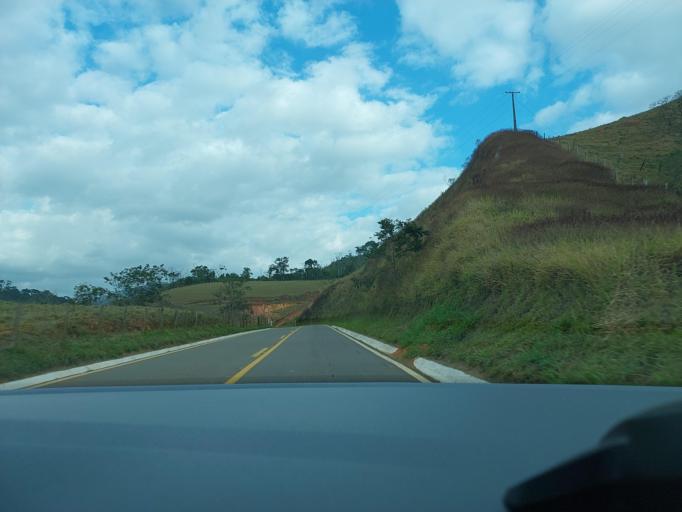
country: BR
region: Minas Gerais
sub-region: Visconde Do Rio Branco
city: Visconde do Rio Branco
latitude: -20.9343
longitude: -42.6319
